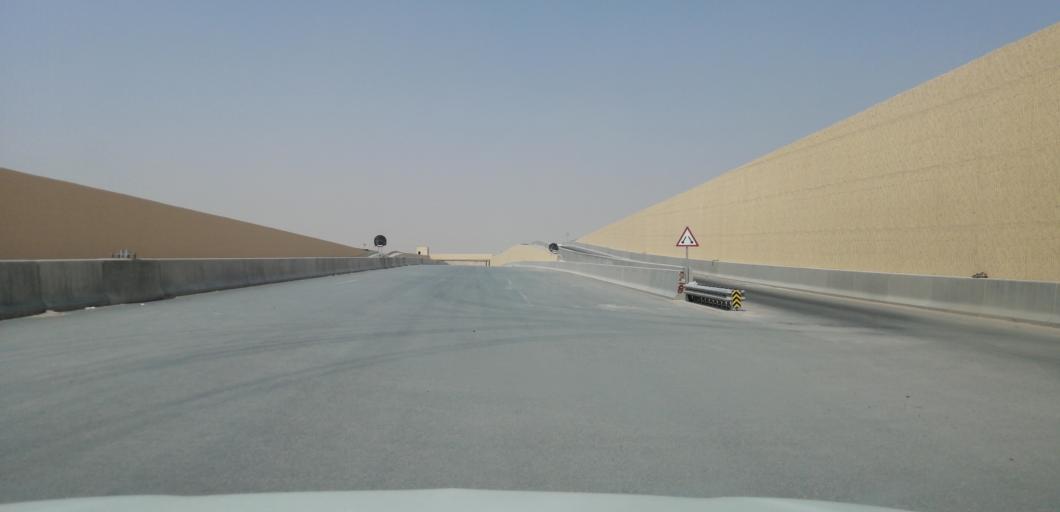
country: KW
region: Muhafazat al Jahra'
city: Al Jahra'
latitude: 29.4538
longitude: 47.5551
